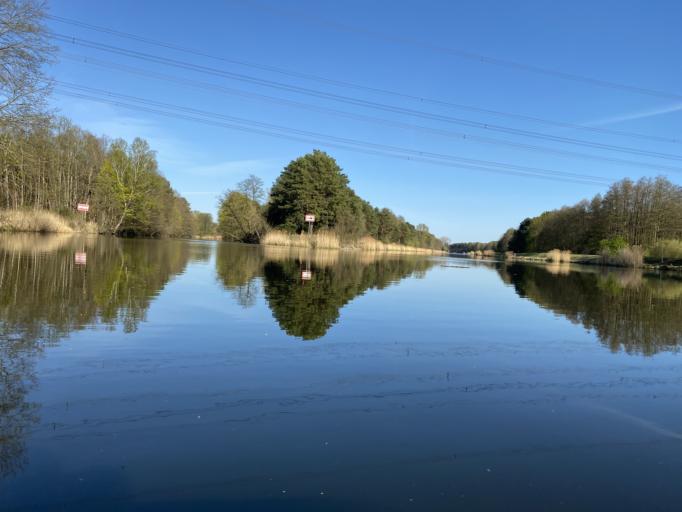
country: DE
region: Brandenburg
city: Mullrose
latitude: 52.2466
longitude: 14.4608
